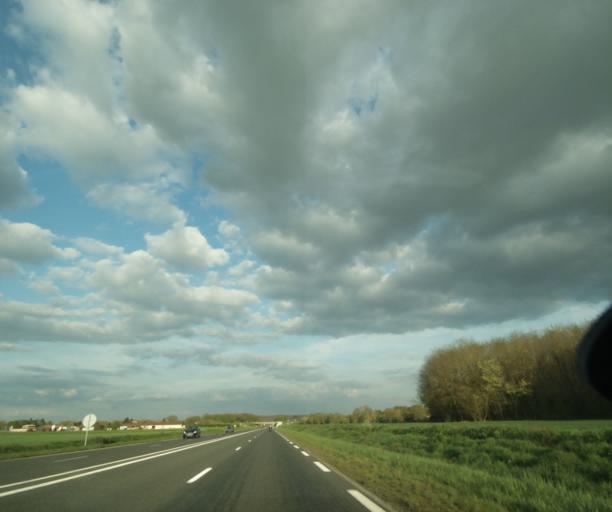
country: FR
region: Ile-de-France
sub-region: Departement de Seine-et-Marne
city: Barbizon
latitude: 48.4565
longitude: 2.5968
